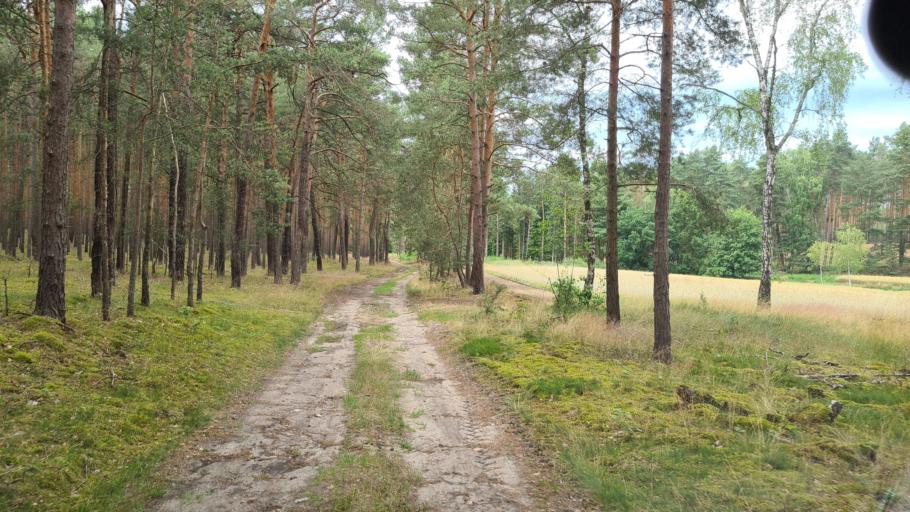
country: DE
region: Brandenburg
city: Bronkow
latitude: 51.7094
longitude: 13.8612
